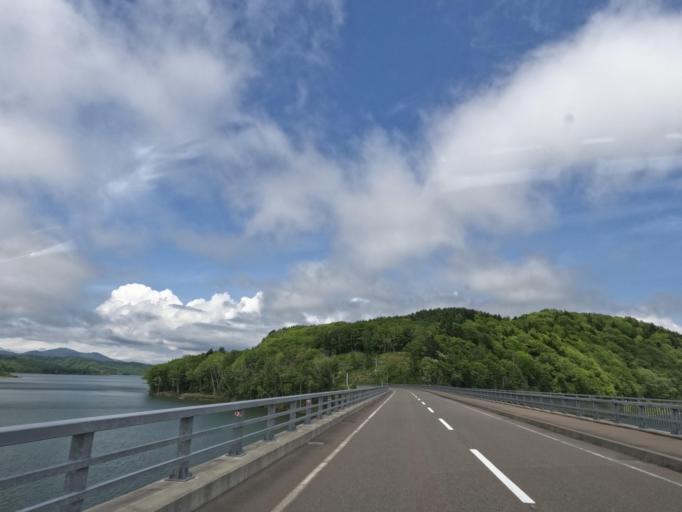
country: JP
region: Hokkaido
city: Tobetsu
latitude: 43.3458
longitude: 141.5662
